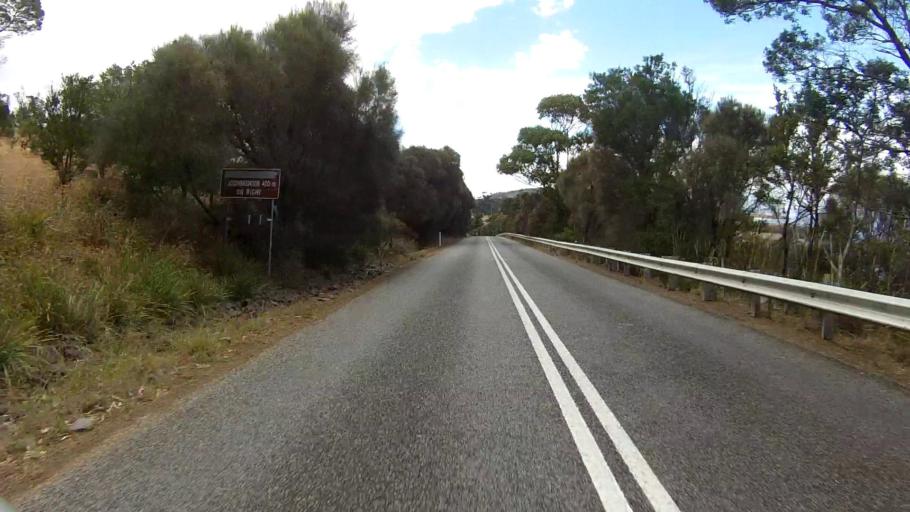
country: AU
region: Tasmania
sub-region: Sorell
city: Sorell
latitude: -42.2197
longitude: 148.0299
